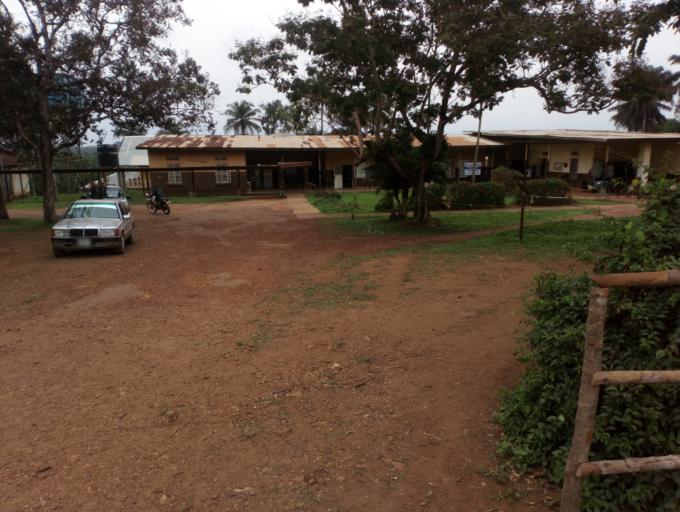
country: SL
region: Southern Province
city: Sumbuya
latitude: 7.6046
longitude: -12.1677
